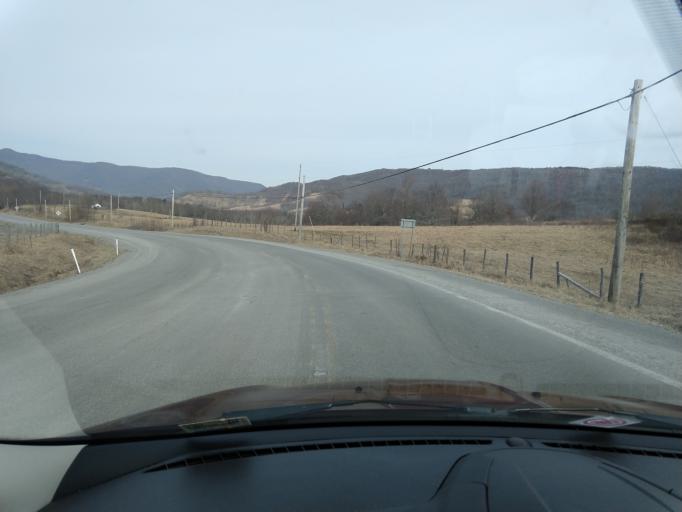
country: US
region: West Virginia
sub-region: Pendleton County
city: Franklin
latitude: 38.8938
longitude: -79.4679
